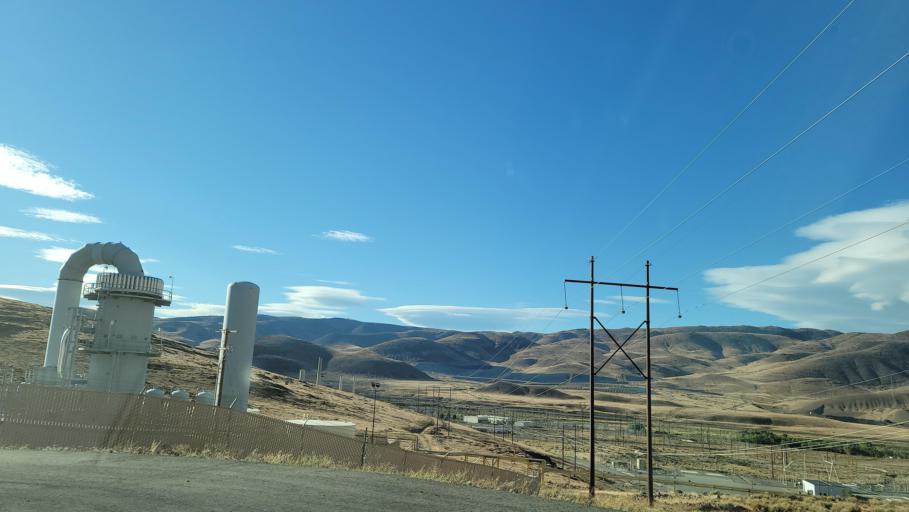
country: US
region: Nevada
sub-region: Washoe County
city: Spanish Springs
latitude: 39.5530
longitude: -119.5179
